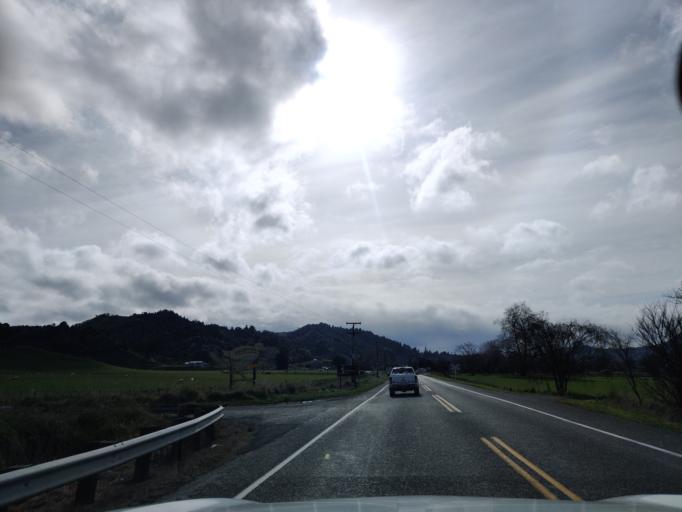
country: NZ
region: Manawatu-Wanganui
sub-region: Ruapehu District
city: Waiouru
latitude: -39.8208
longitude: 175.7775
